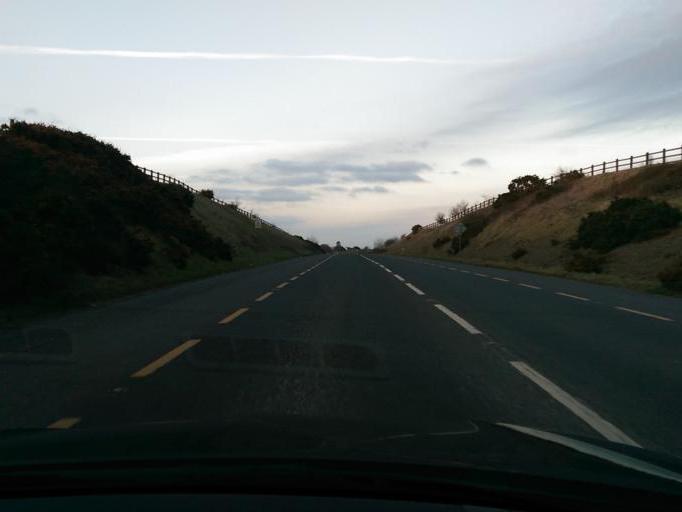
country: IE
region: Munster
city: Nenagh Bridge
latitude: 52.9431
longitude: -8.1475
